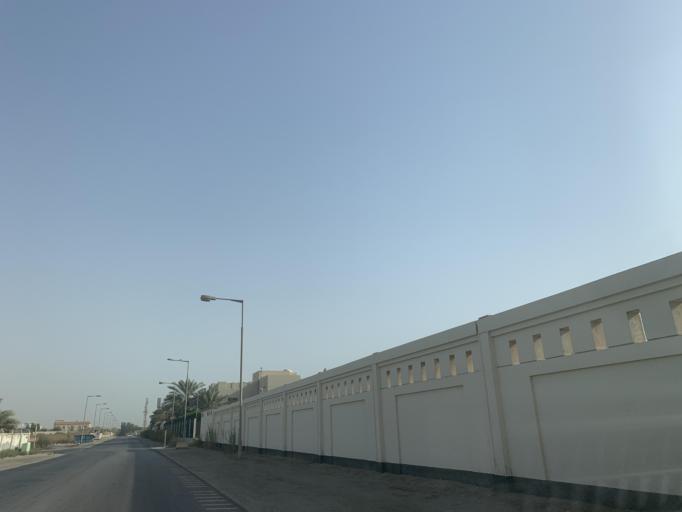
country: BH
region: Central Governorate
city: Madinat Hamad
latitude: 26.1798
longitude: 50.4678
